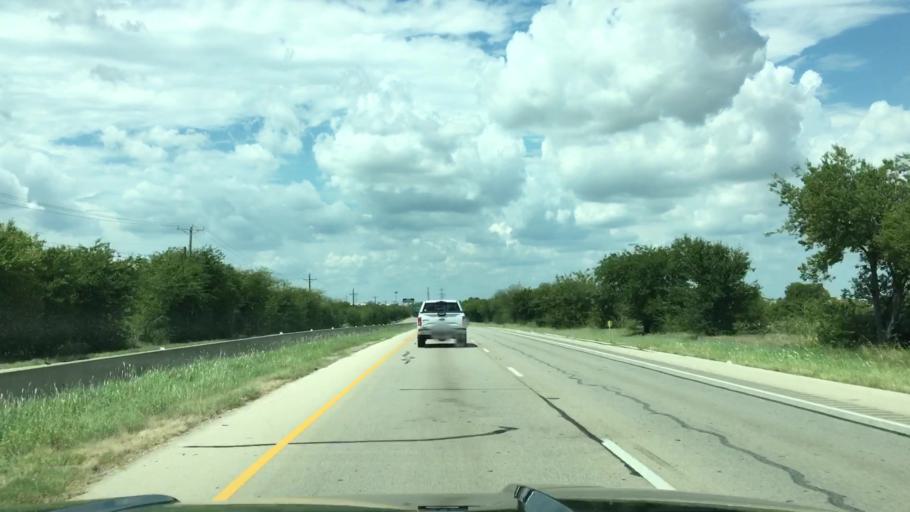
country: US
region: Texas
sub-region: Tarrant County
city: Saginaw
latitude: 32.8940
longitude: -97.3931
